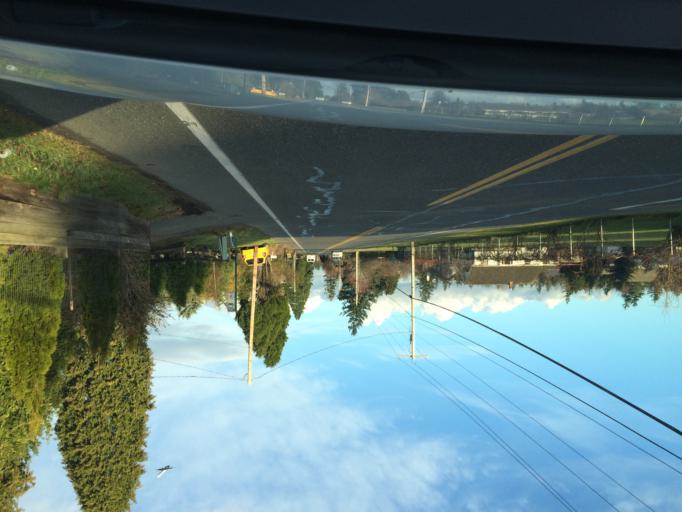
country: US
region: Washington
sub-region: Whatcom County
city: Ferndale
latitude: 48.8413
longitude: -122.5409
